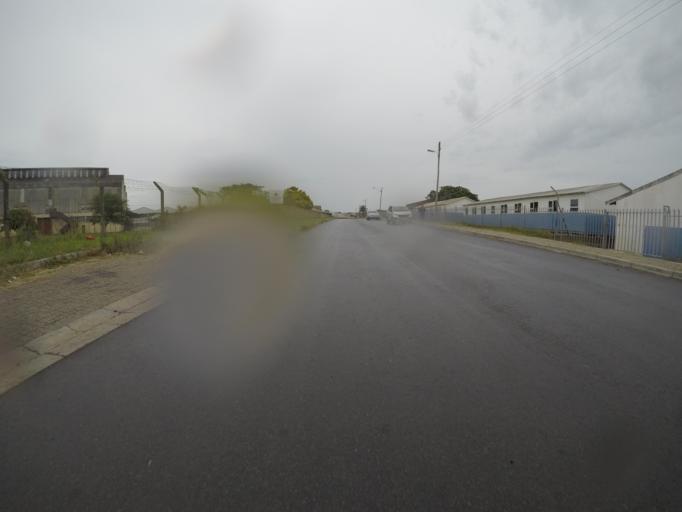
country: ZA
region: Eastern Cape
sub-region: Buffalo City Metropolitan Municipality
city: East London
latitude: -32.9722
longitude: 27.8228
